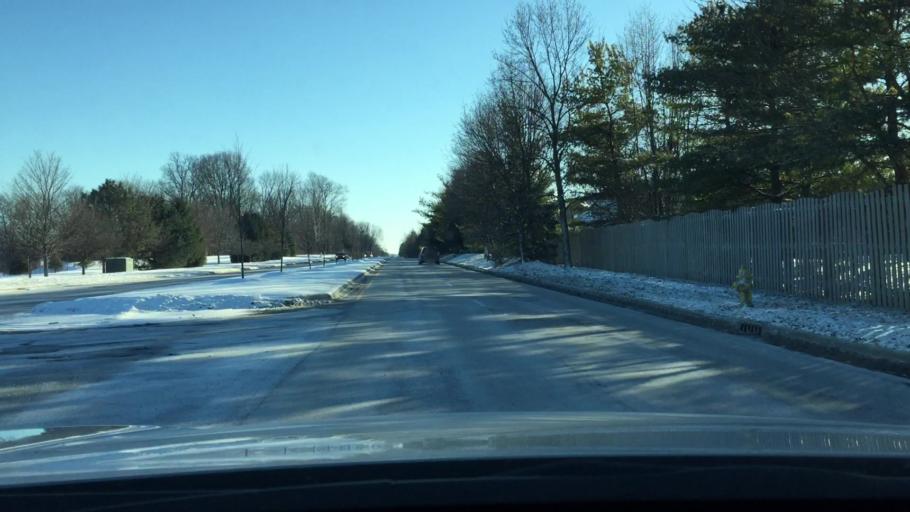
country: US
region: Indiana
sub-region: Hamilton County
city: Carmel
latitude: 39.9988
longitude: -86.0706
